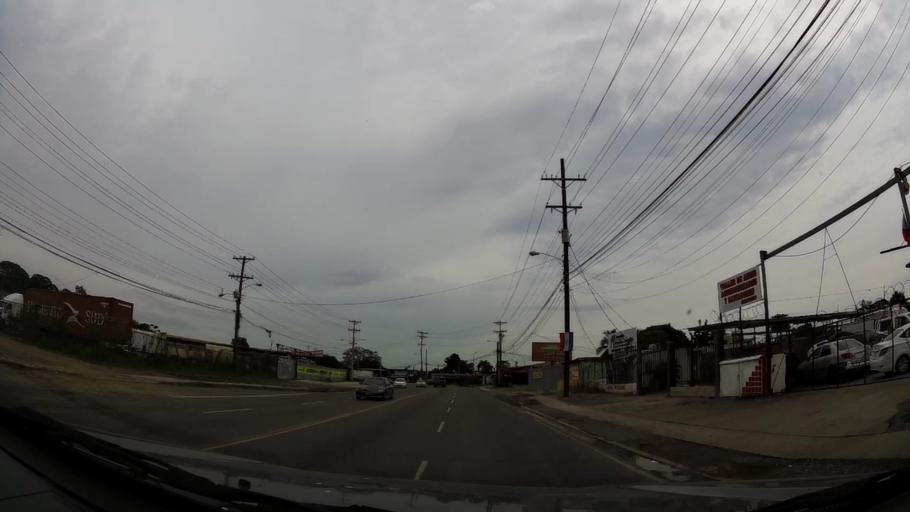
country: PA
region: Panama
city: San Miguelito
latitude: 9.0465
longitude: -79.4426
